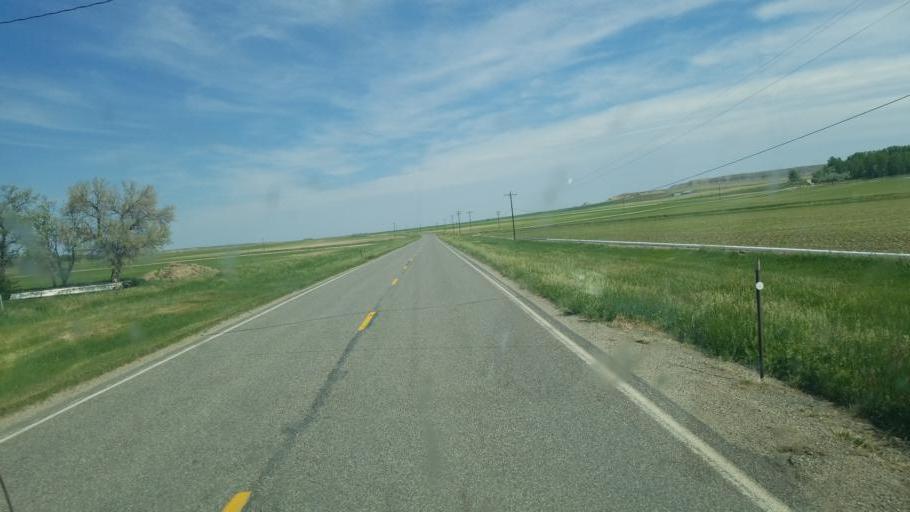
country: US
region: Wyoming
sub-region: Park County
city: Powell
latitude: 44.7649
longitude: -108.9314
